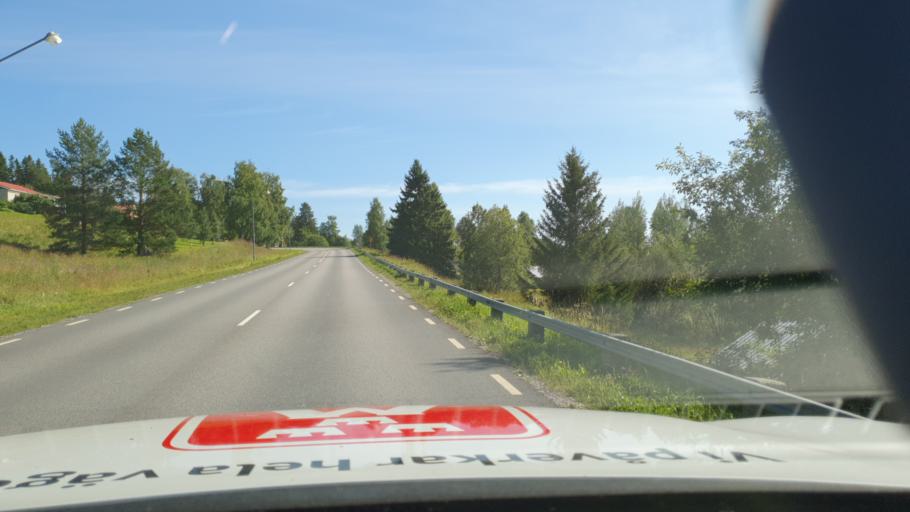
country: SE
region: Jaemtland
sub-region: Krokoms Kommun
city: Krokom
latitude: 63.6724
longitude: 14.5957
